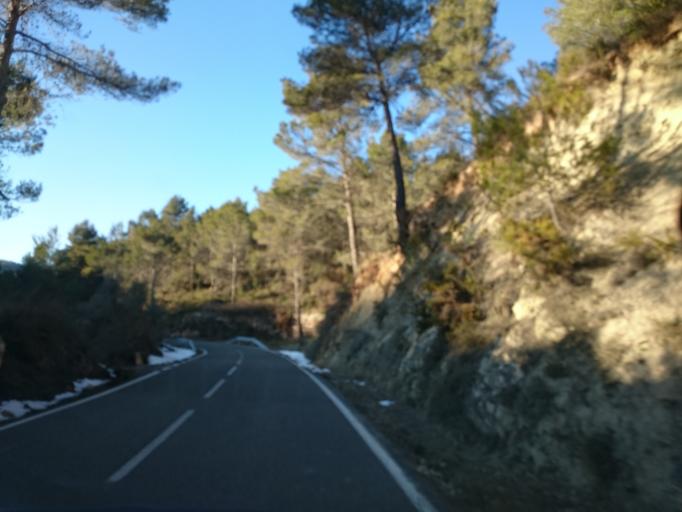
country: ES
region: Catalonia
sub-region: Provincia de Tarragona
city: la Bisbal del Penedes
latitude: 41.3769
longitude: 1.4803
